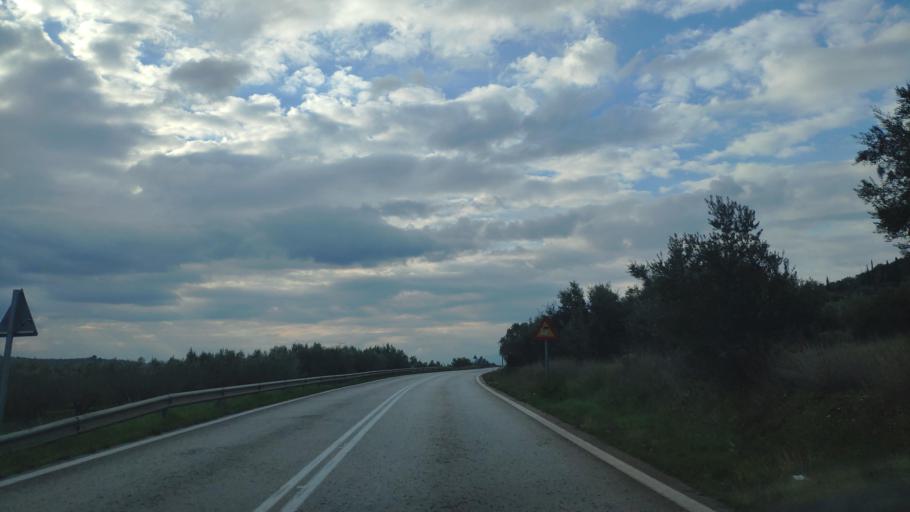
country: GR
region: Peloponnese
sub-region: Nomos Argolidos
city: Koutsopodi
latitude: 37.7376
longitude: 22.7365
